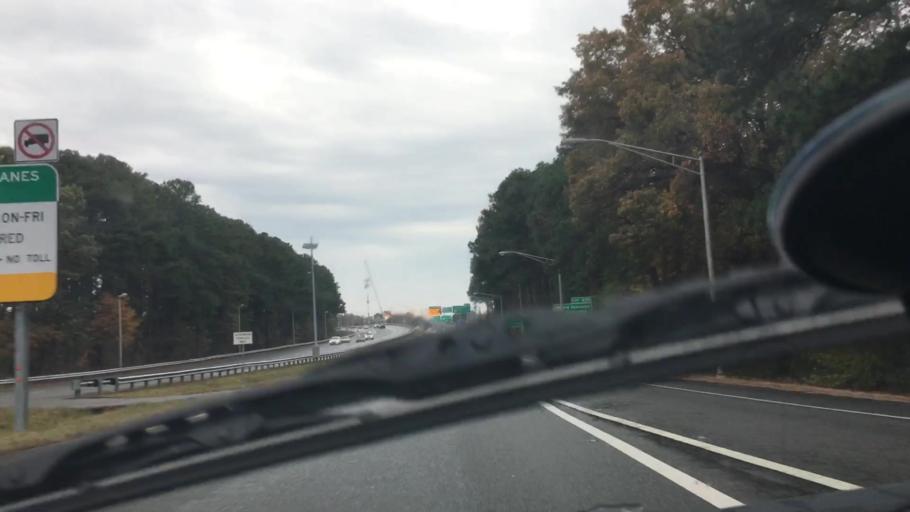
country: US
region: Virginia
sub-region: City of Norfolk
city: Norfolk
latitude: 36.9261
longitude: -76.2695
